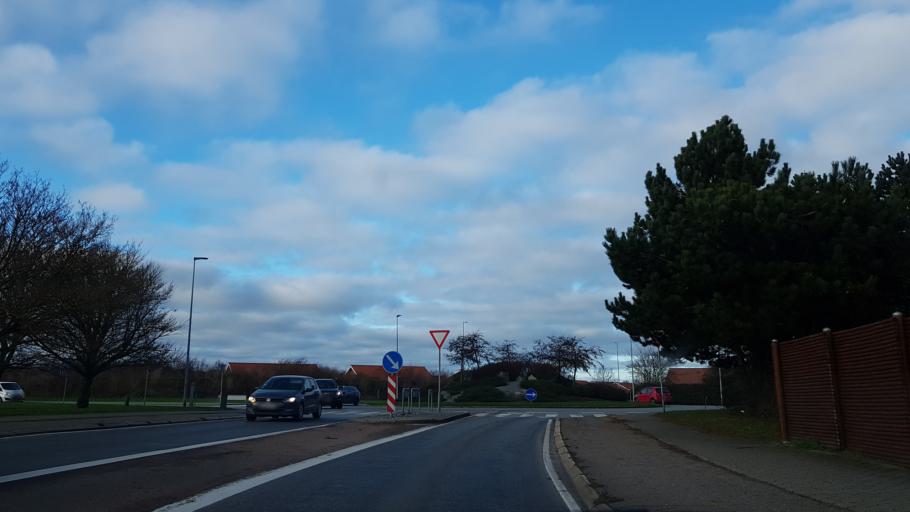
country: DK
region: Zealand
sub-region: Slagelse Kommune
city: Slagelse
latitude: 55.3898
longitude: 11.3282
